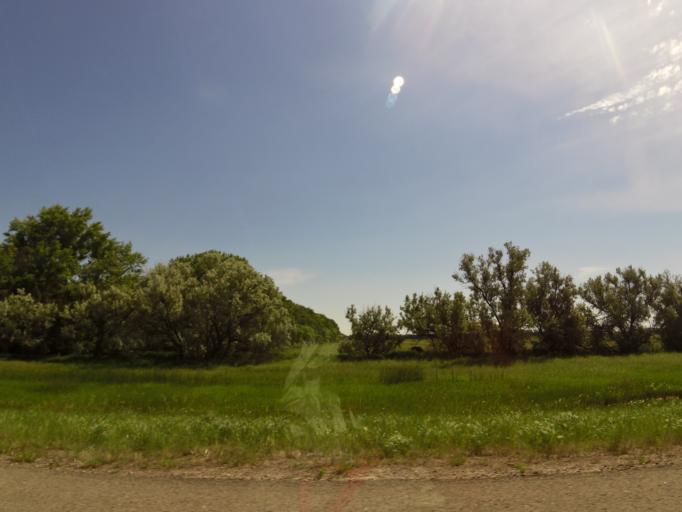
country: US
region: North Dakota
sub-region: Traill County
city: Hillsboro
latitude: 47.6643
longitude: -97.0803
